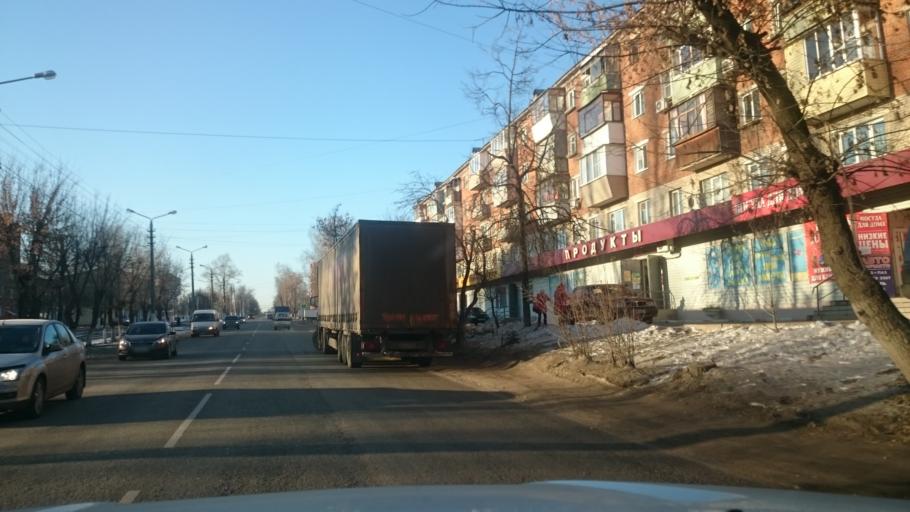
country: RU
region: Tula
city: Tula
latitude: 54.2153
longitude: 37.6709
